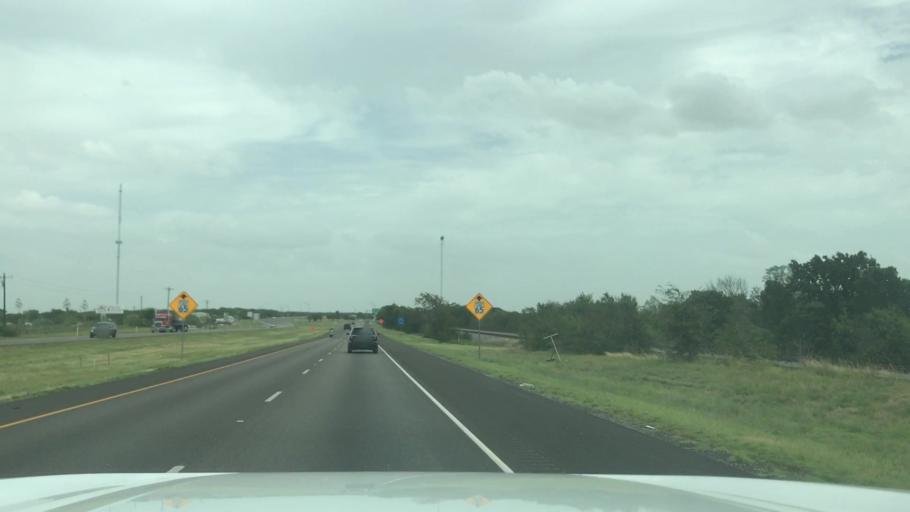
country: US
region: Texas
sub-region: McLennan County
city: Riesel
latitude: 31.5178
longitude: -96.9687
